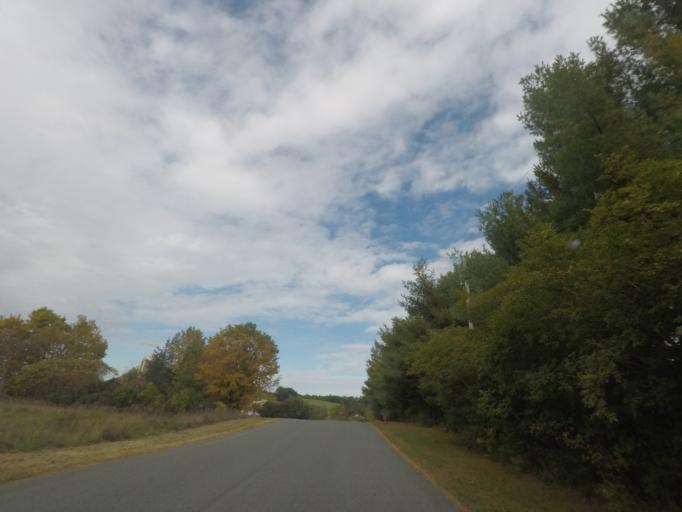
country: US
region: New York
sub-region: Rensselaer County
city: Nassau
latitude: 42.5306
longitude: -73.6441
